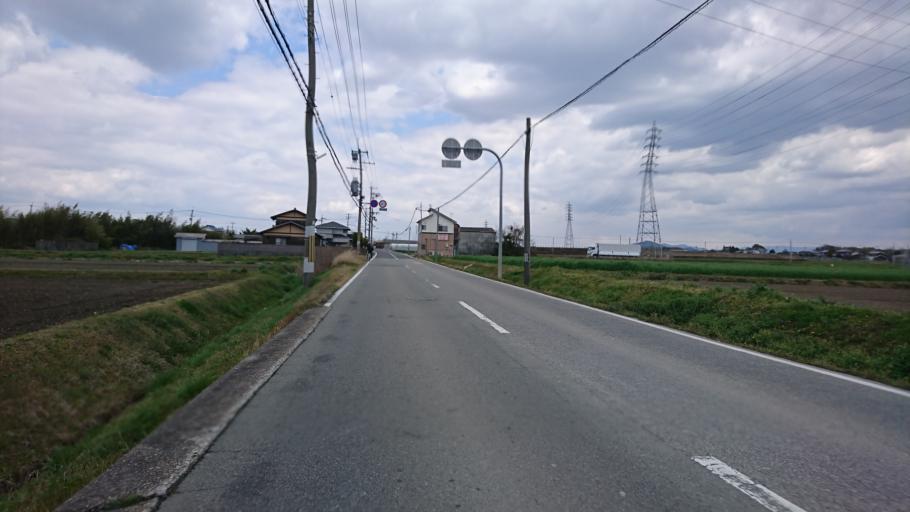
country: JP
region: Hyogo
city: Miki
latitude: 34.7420
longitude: 134.9320
